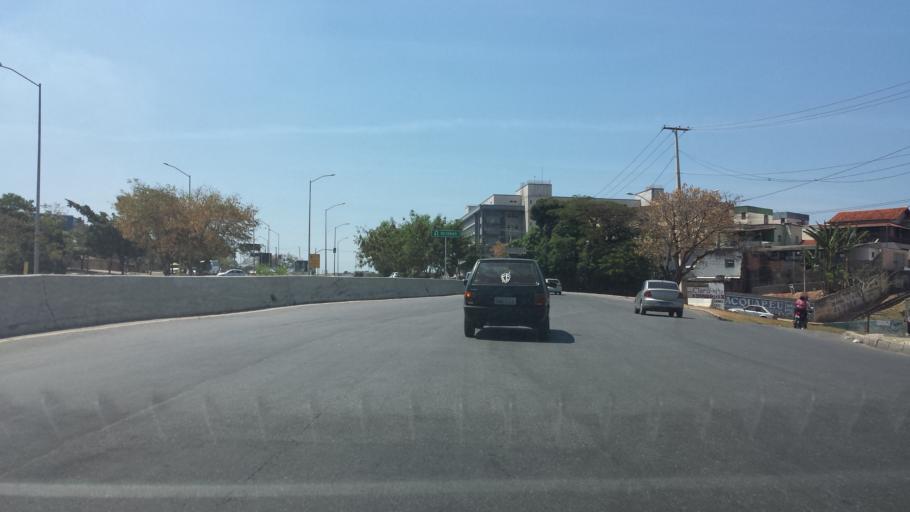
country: BR
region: Minas Gerais
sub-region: Belo Horizonte
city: Belo Horizonte
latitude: -19.8193
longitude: -43.9508
